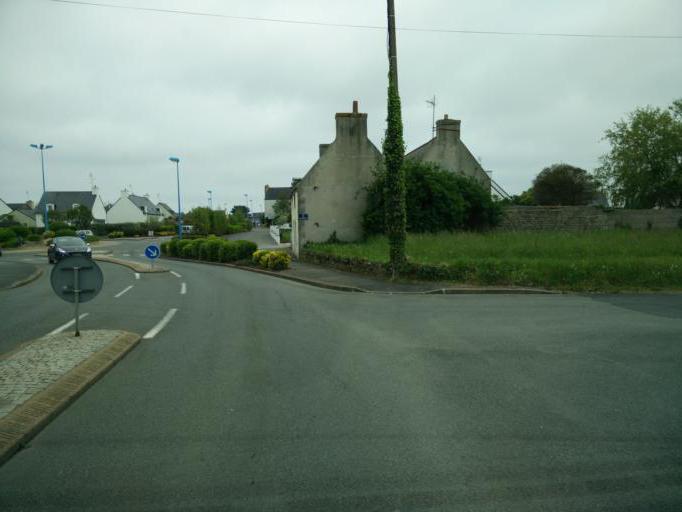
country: FR
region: Brittany
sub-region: Departement du Finistere
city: Plobannalec-Lesconil
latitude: 47.8028
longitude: -4.2222
